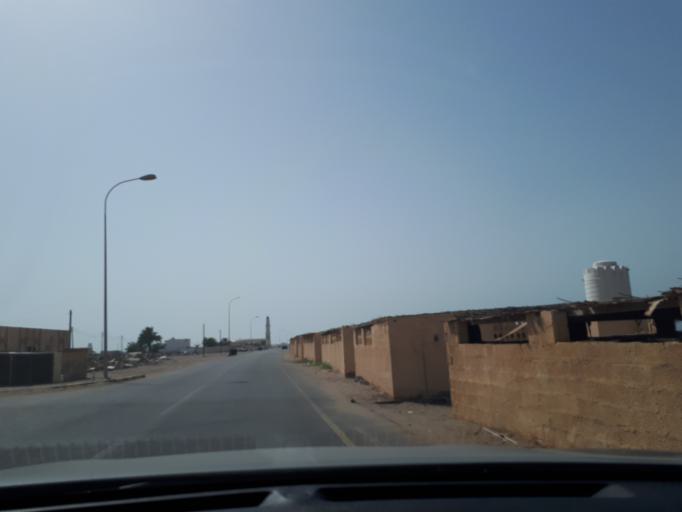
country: OM
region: Al Batinah
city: Barka'
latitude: 23.7198
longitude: 57.8568
